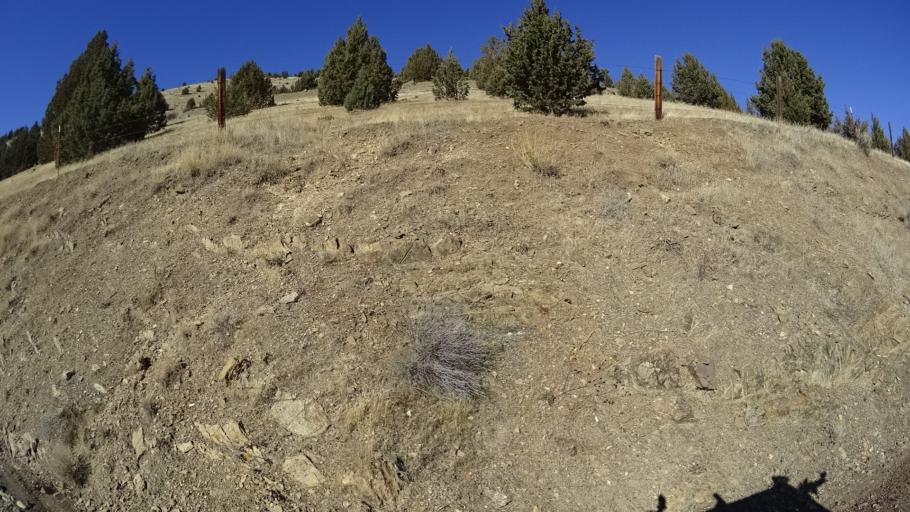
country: US
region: California
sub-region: Siskiyou County
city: Weed
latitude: 41.4882
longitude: -122.5657
